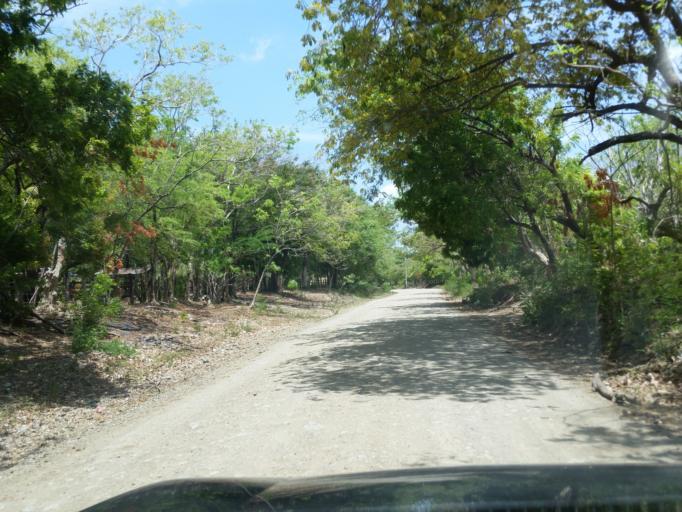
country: NI
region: Rivas
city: Tola
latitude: 11.5181
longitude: -86.0762
